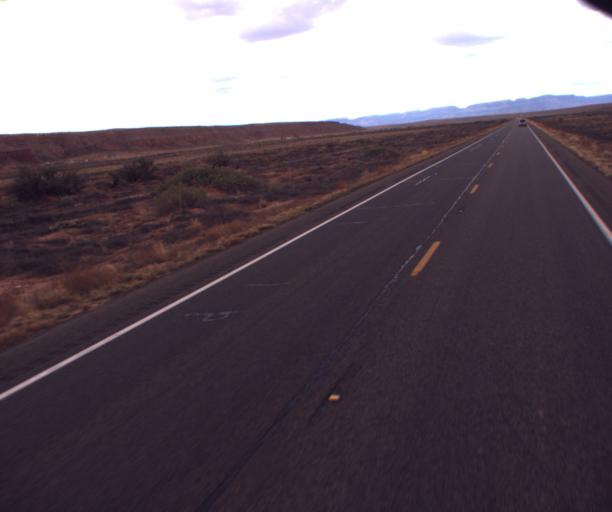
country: US
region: Arizona
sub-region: Navajo County
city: Kayenta
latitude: 36.7679
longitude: -110.0304
